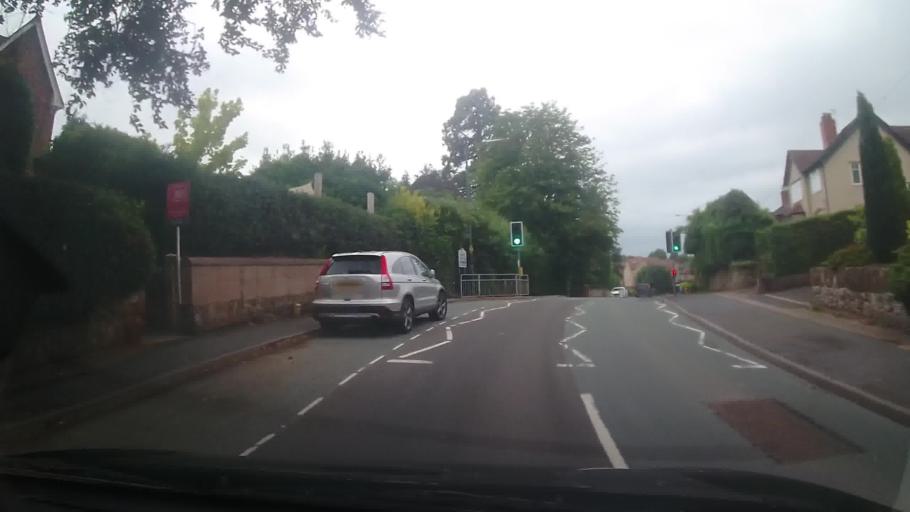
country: GB
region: England
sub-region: Shropshire
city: Shrewsbury
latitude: 52.7109
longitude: -2.7746
